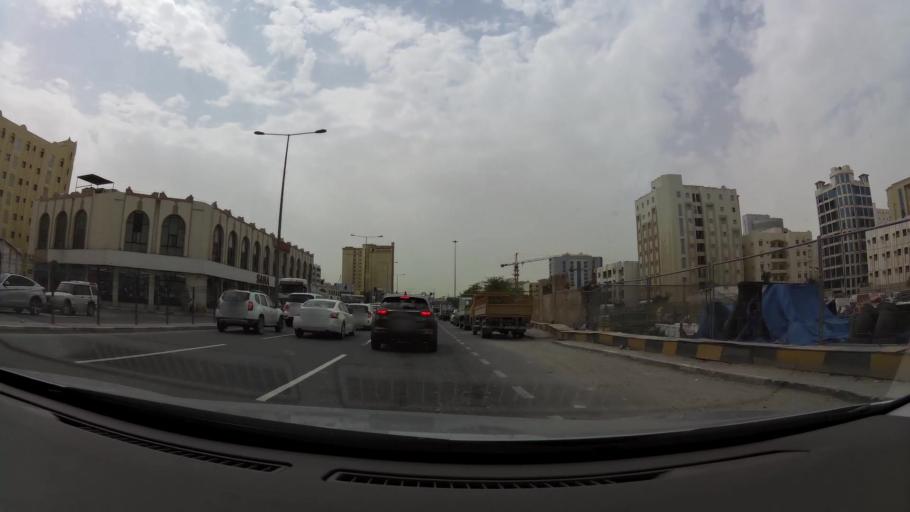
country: QA
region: Baladiyat ad Dawhah
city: Doha
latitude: 25.2831
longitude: 51.5465
